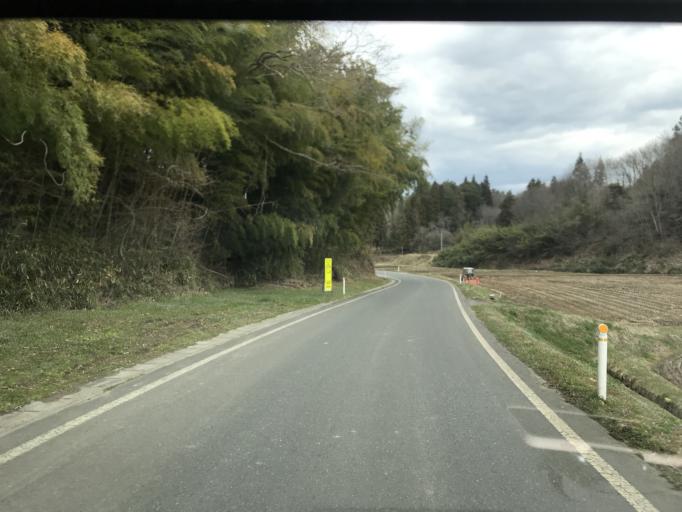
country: JP
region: Iwate
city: Ichinoseki
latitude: 38.9563
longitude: 141.0890
